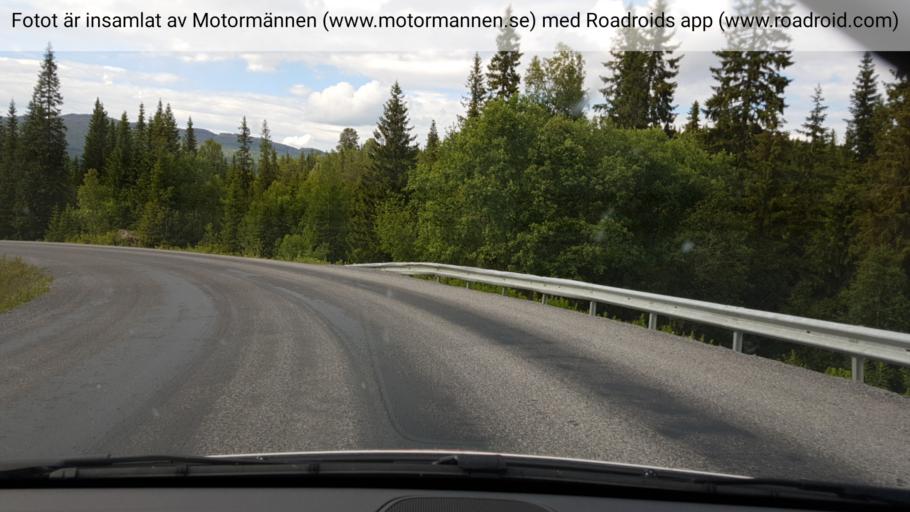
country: NO
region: Nord-Trondelag
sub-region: Meraker
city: Meraker
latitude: 63.6488
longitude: 12.2639
